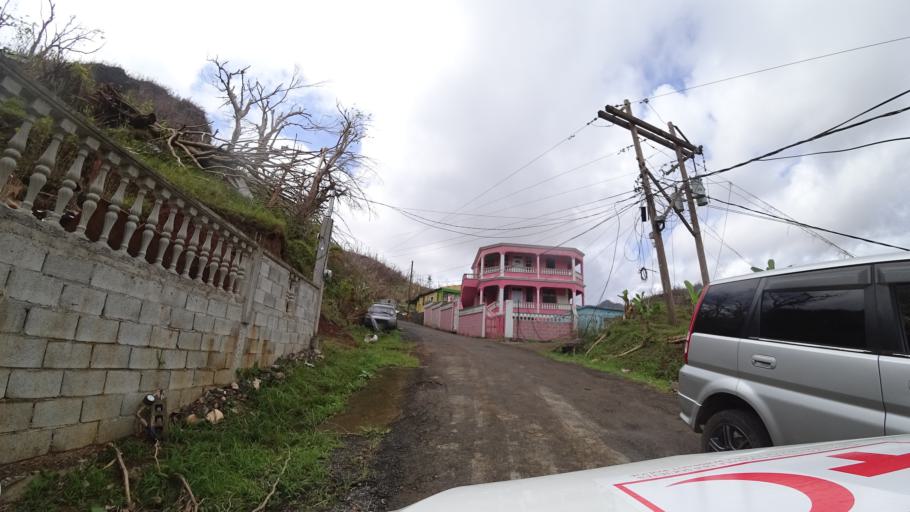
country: DM
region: Saint David
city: Castle Bruce
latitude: 15.4016
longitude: -61.2554
